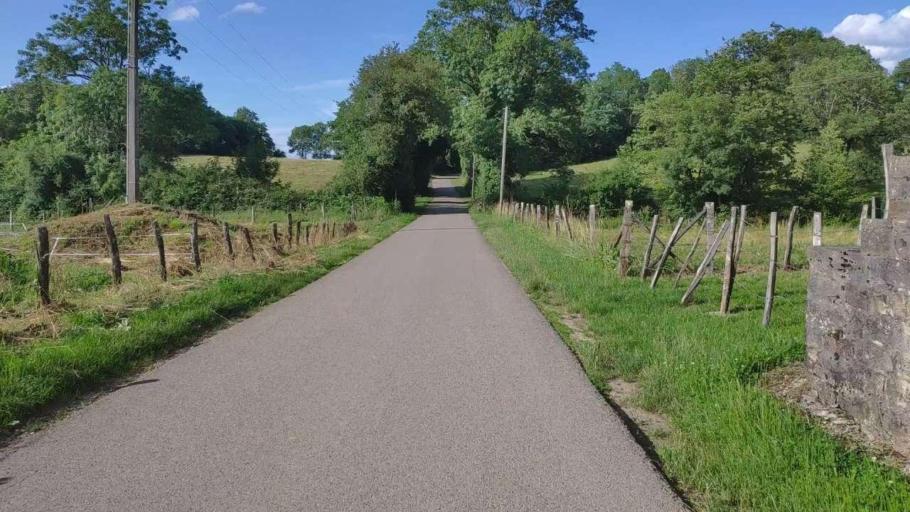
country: FR
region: Franche-Comte
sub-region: Departement du Jura
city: Bletterans
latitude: 46.7528
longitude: 5.5246
